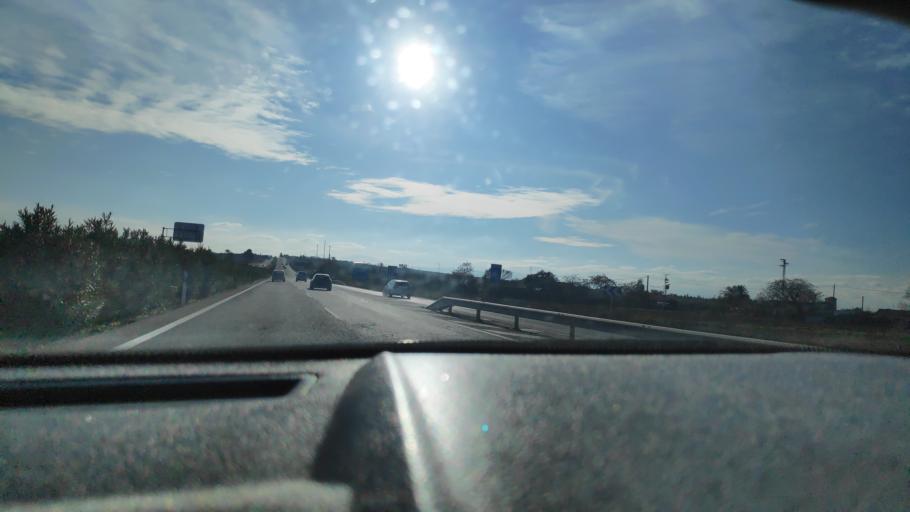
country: ES
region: Andalusia
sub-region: Province of Cordoba
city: La Carlota
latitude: 37.6009
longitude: -4.9733
